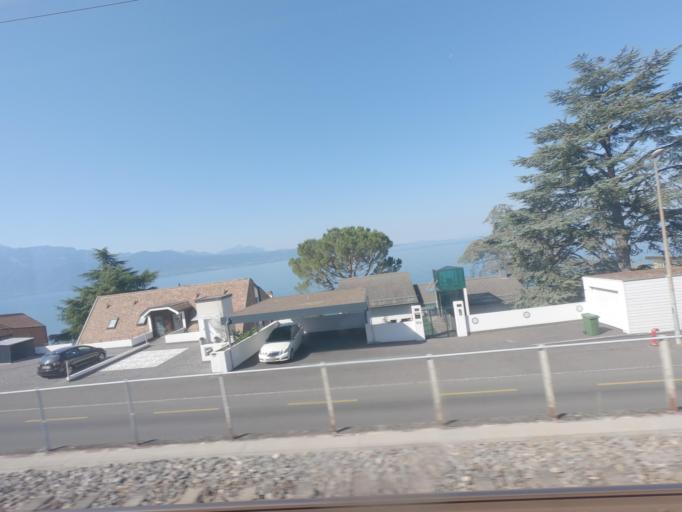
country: CH
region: Vaud
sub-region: Lavaux-Oron District
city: Cully
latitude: 46.4938
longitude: 6.7102
